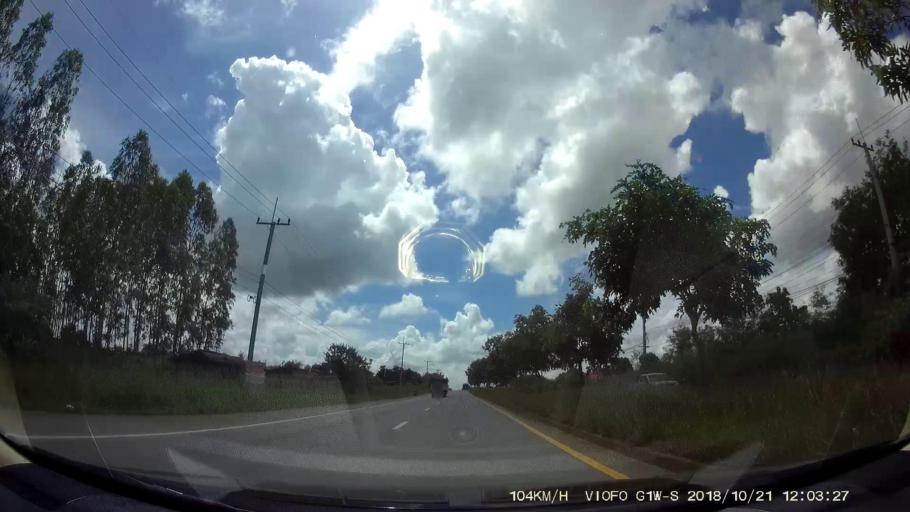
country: TH
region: Chaiyaphum
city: Chatturat
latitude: 15.5089
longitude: 101.8221
